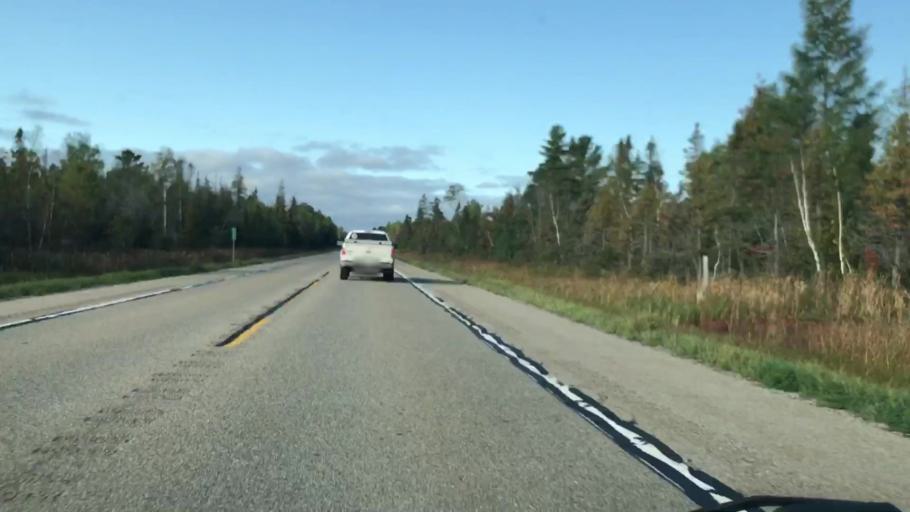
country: US
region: Michigan
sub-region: Luce County
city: Newberry
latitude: 46.3144
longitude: -85.2025
